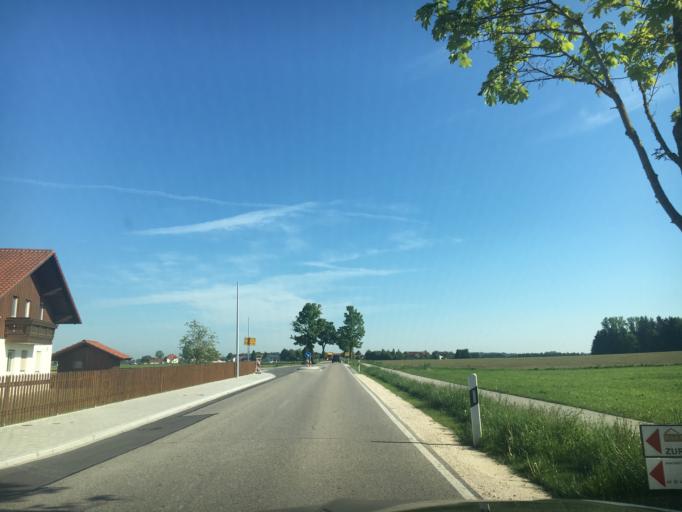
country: DE
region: Bavaria
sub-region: Upper Bavaria
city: Tacherting
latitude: 48.0824
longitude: 12.5956
